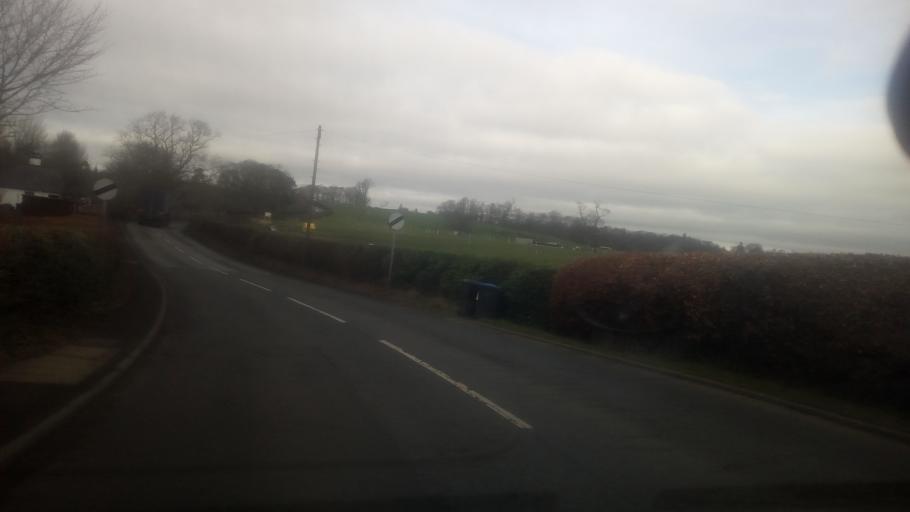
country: GB
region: Scotland
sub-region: The Scottish Borders
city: Kelso
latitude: 55.5951
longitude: -2.4465
